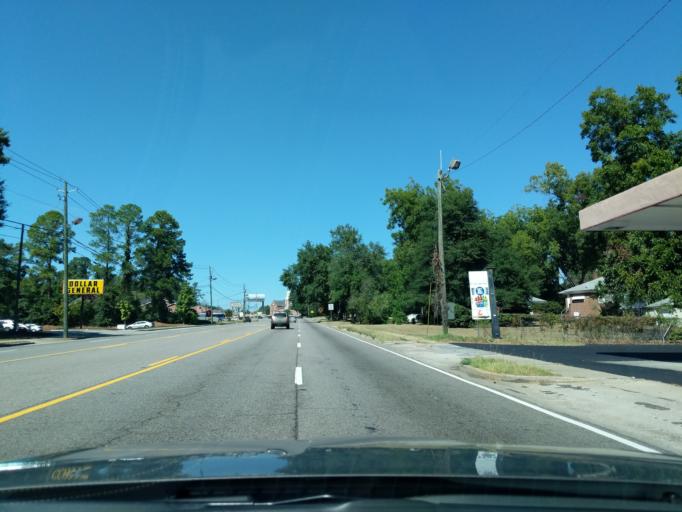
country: US
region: Georgia
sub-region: Richmond County
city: Augusta
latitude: 33.4964
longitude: -82.0108
